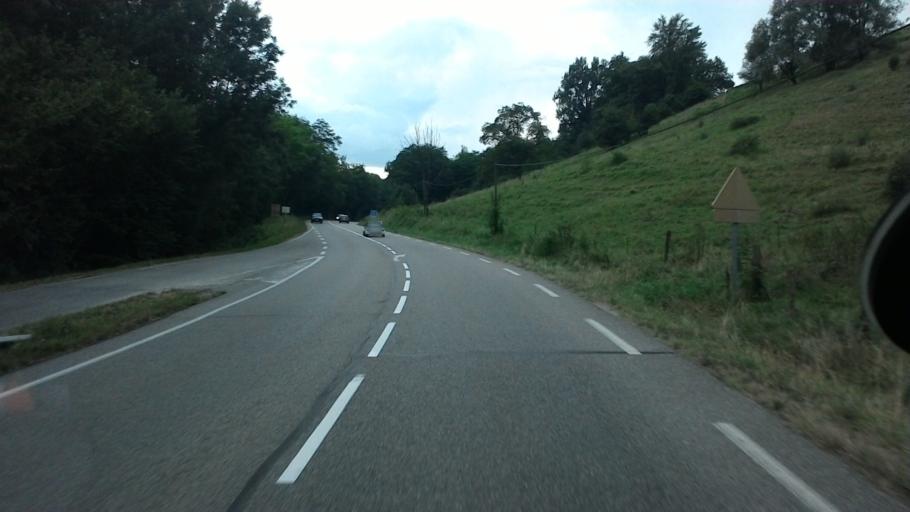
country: FR
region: Rhone-Alpes
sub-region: Departement de la Savoie
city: Yenne
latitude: 45.7032
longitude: 5.7877
